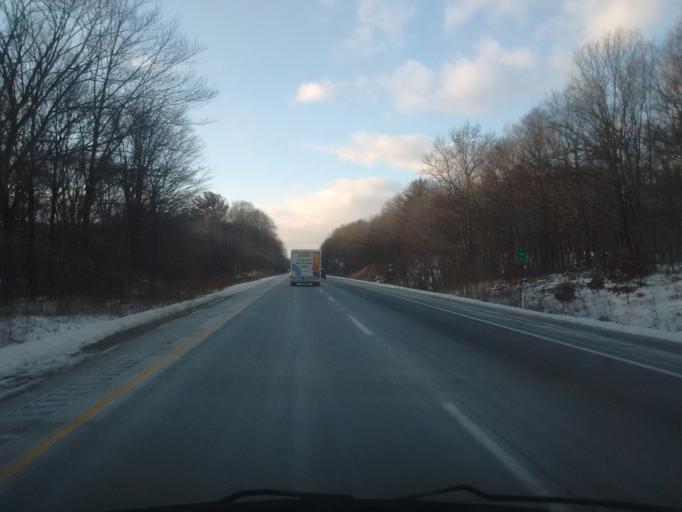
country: US
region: Pennsylvania
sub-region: Pike County
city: Milford
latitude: 41.3363
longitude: -74.8623
